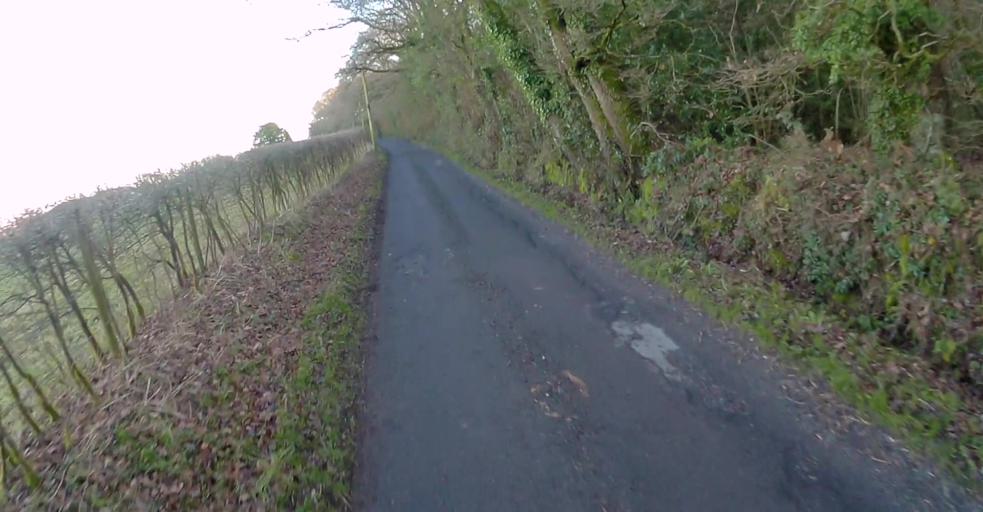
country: GB
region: England
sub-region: Hampshire
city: Hook
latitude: 51.3194
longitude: -0.9739
